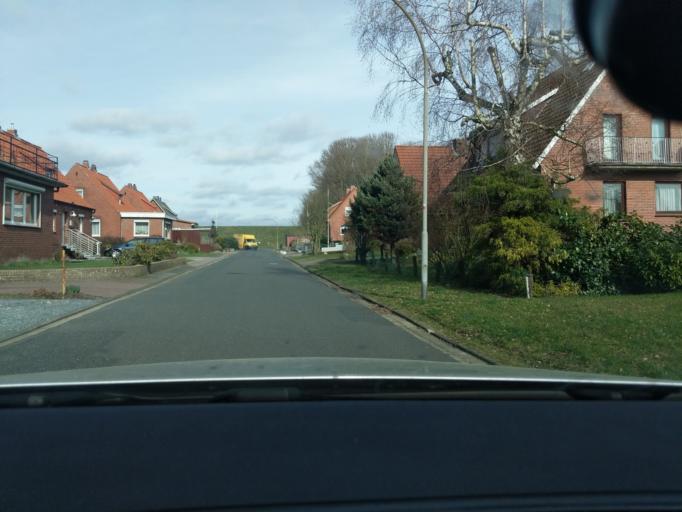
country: DE
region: Lower Saxony
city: Drochtersen
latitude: 53.7113
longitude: 9.3944
